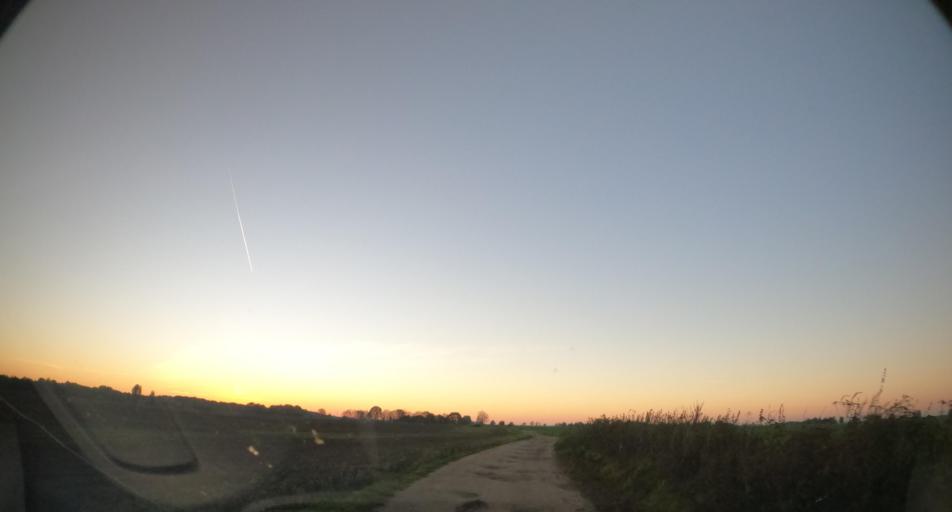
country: DE
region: Mecklenburg-Vorpommern
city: Ducherow
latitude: 53.7799
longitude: 13.8529
